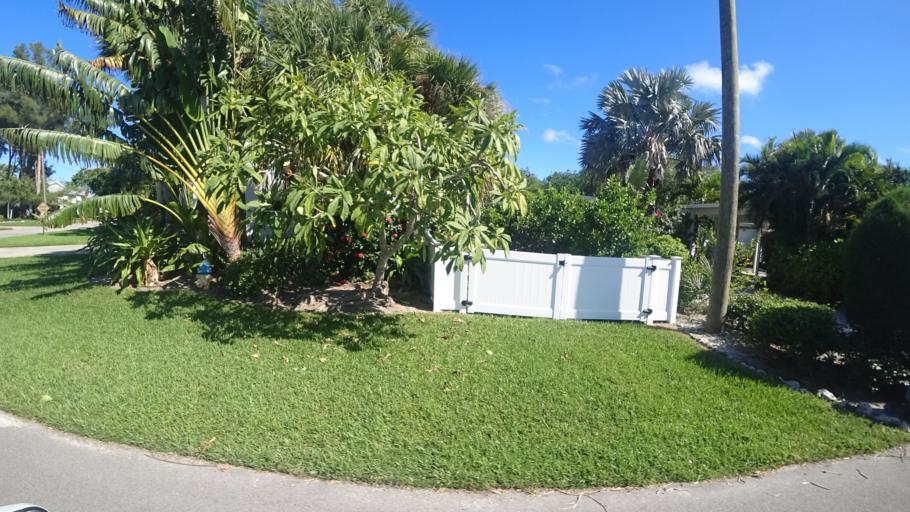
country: US
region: Florida
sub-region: Manatee County
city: Holmes Beach
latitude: 27.5100
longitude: -82.7137
